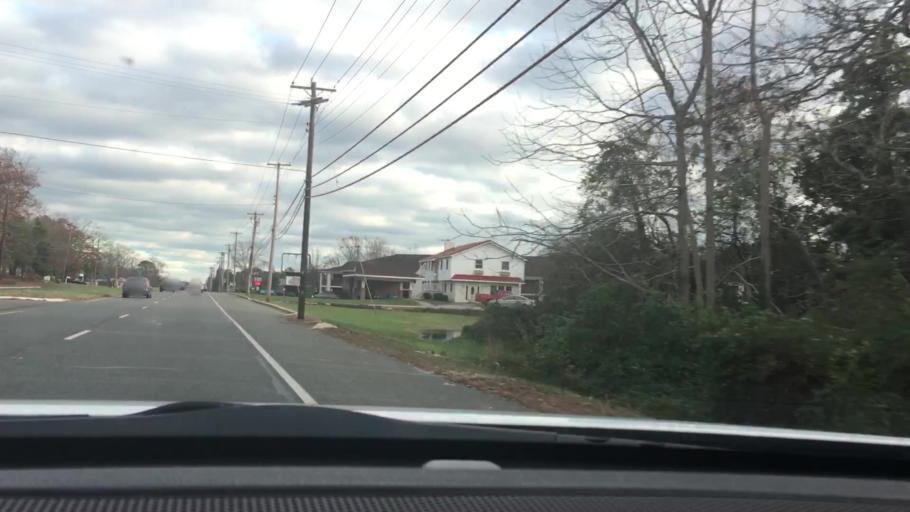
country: US
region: New Jersey
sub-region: Atlantic County
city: Northfield
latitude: 39.4146
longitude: -74.5762
